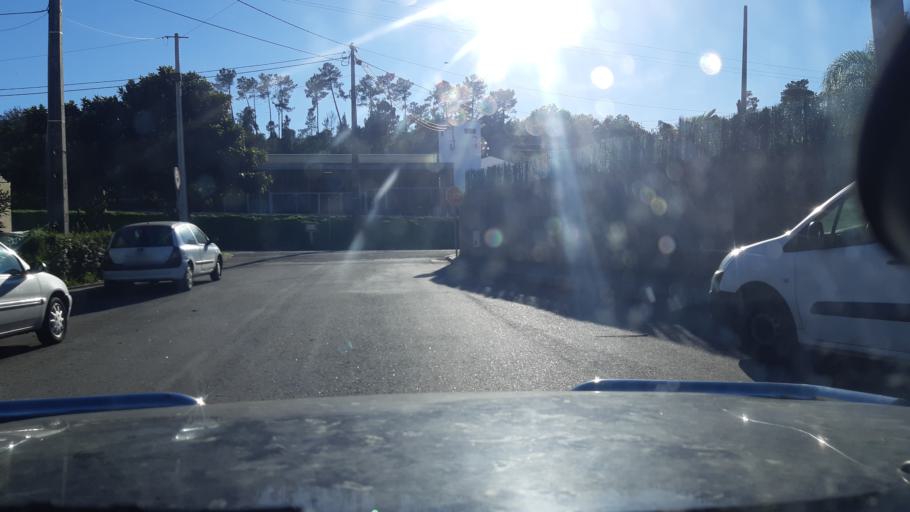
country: PT
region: Aveiro
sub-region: Agueda
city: Agueda
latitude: 40.5630
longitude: -8.4444
